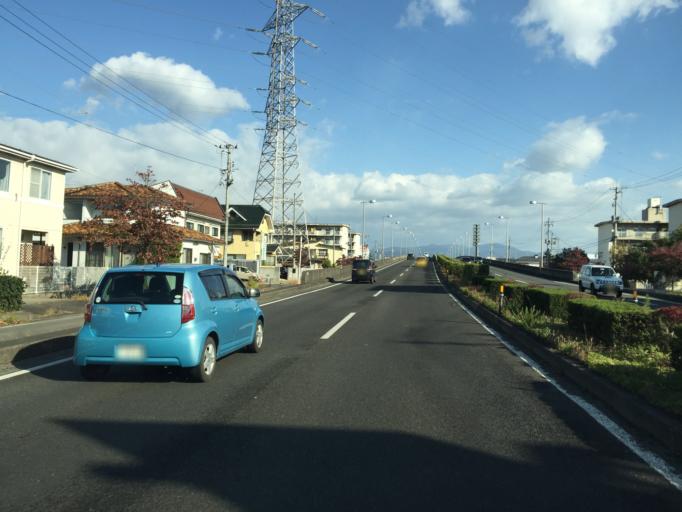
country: JP
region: Fukushima
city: Fukushima-shi
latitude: 37.7622
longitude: 140.4354
